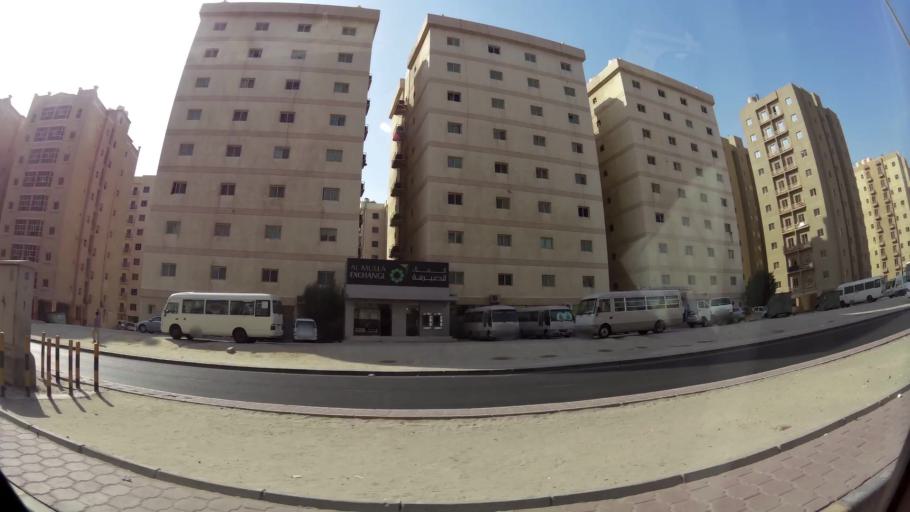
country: KW
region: Al Ahmadi
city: Al Fintas
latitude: 29.1573
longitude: 48.1161
